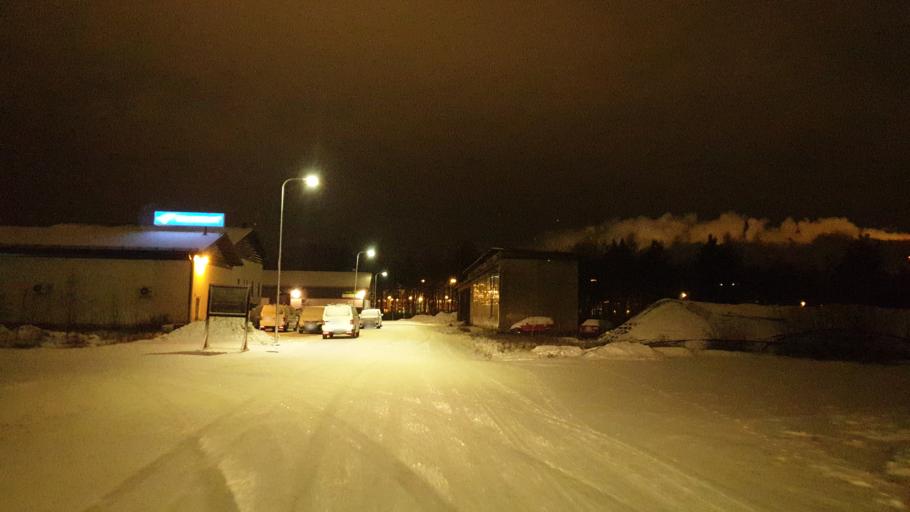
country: FI
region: Northern Ostrobothnia
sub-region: Oulu
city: Oulu
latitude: 64.9954
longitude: 25.4409
